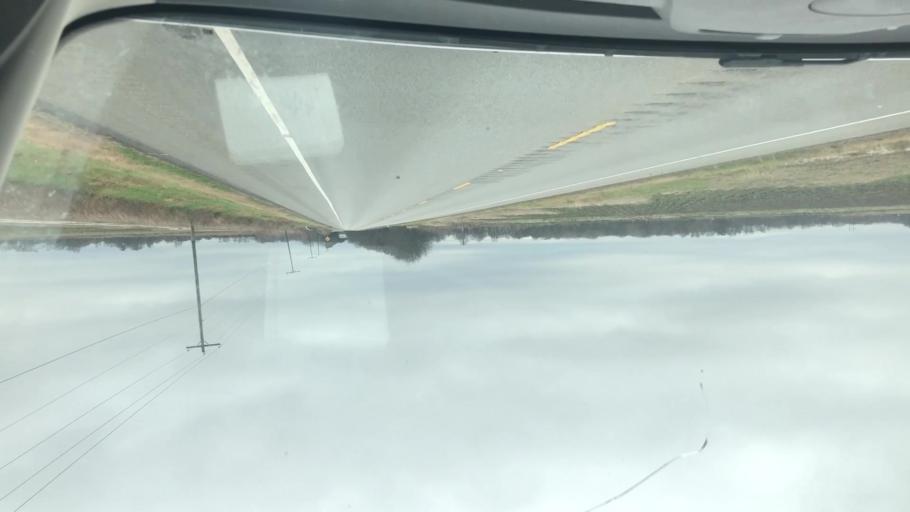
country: US
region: Texas
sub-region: Matagorda County
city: Bay City
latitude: 29.0670
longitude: -95.9709
